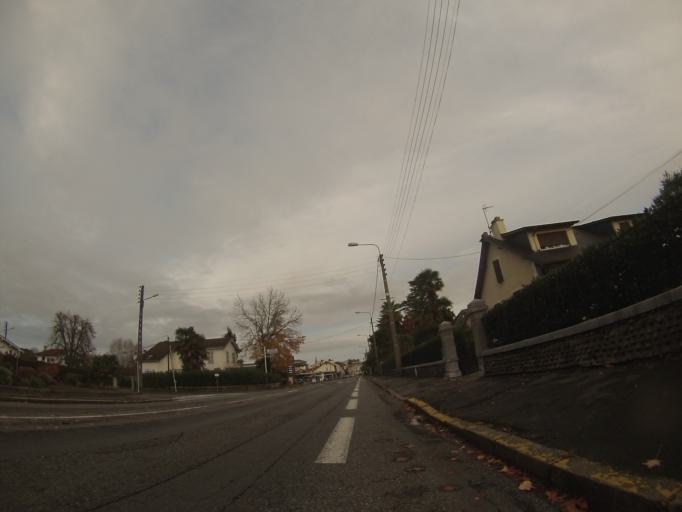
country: FR
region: Aquitaine
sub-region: Departement des Pyrenees-Atlantiques
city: Jurancon
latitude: 43.2850
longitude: -0.3840
